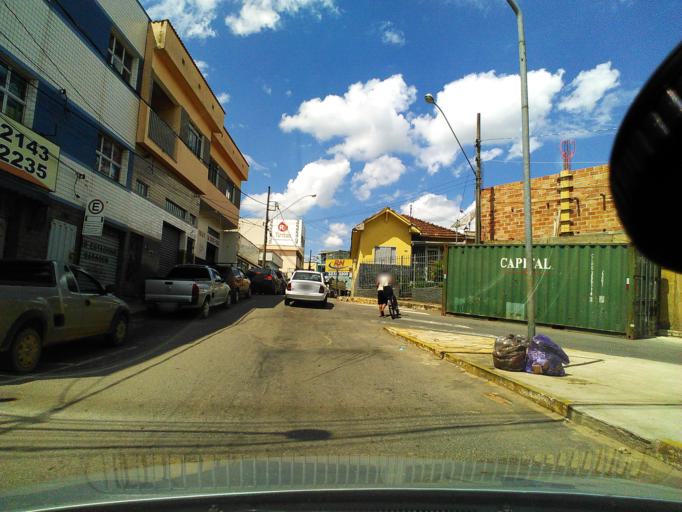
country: BR
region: Minas Gerais
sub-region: Tres Coracoes
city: Tres Coracoes
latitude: -21.6955
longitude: -45.2590
